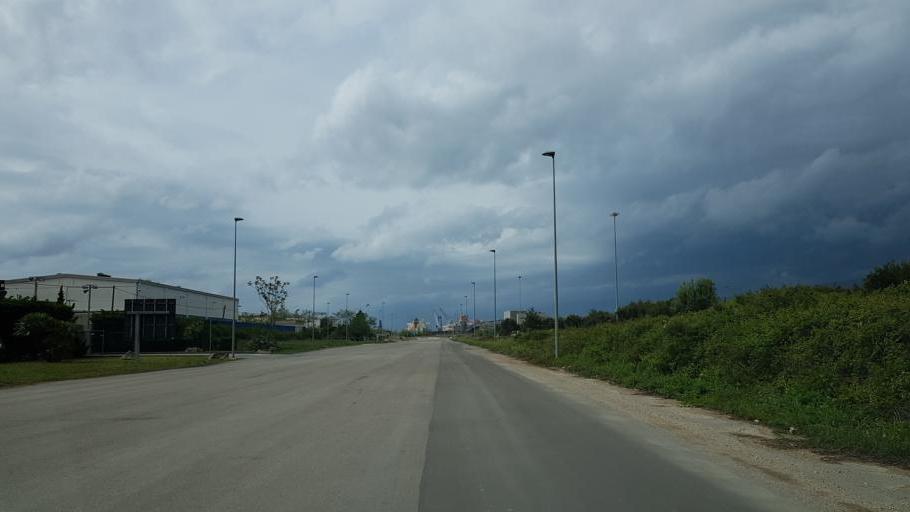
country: IT
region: Apulia
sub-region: Provincia di Brindisi
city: Materdomini
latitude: 40.6387
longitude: 17.9752
